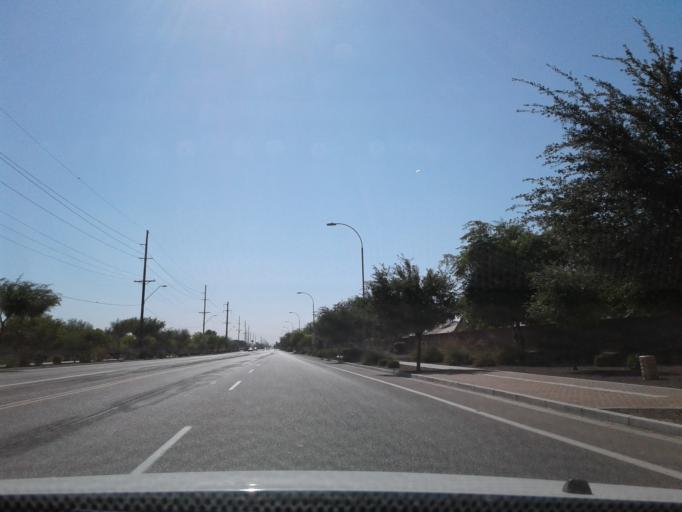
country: US
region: Arizona
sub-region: Maricopa County
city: Laveen
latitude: 33.3919
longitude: -112.1764
